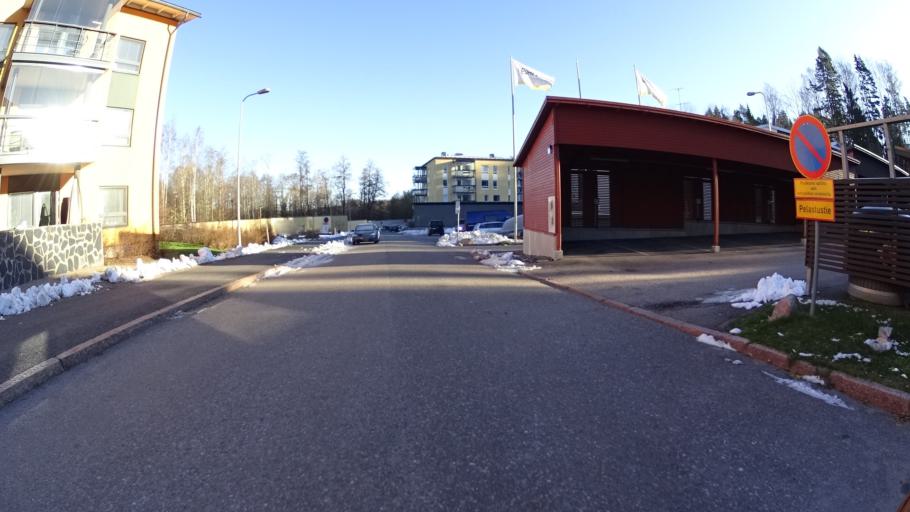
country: FI
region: Uusimaa
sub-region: Helsinki
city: Kauniainen
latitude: 60.2233
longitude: 24.7106
